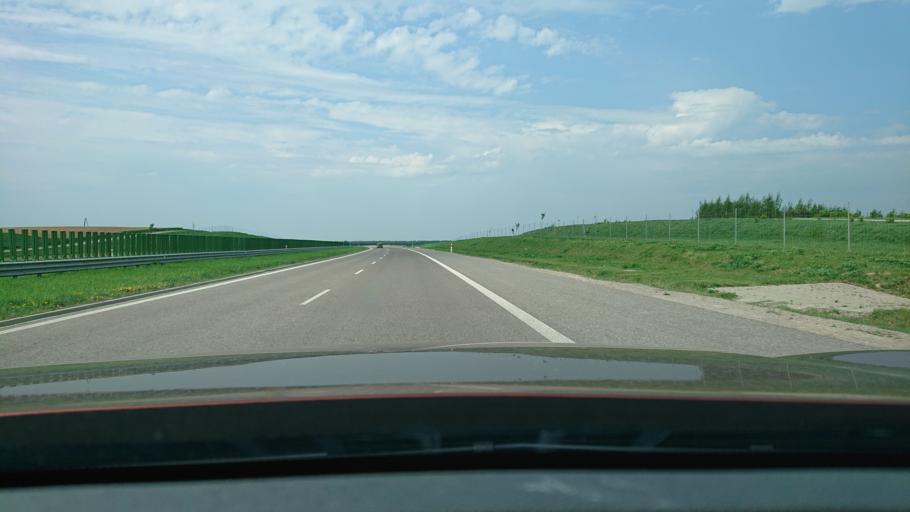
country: PL
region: Subcarpathian Voivodeship
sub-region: Powiat jaroslawski
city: Pawlosiow
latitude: 49.9602
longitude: 22.6592
